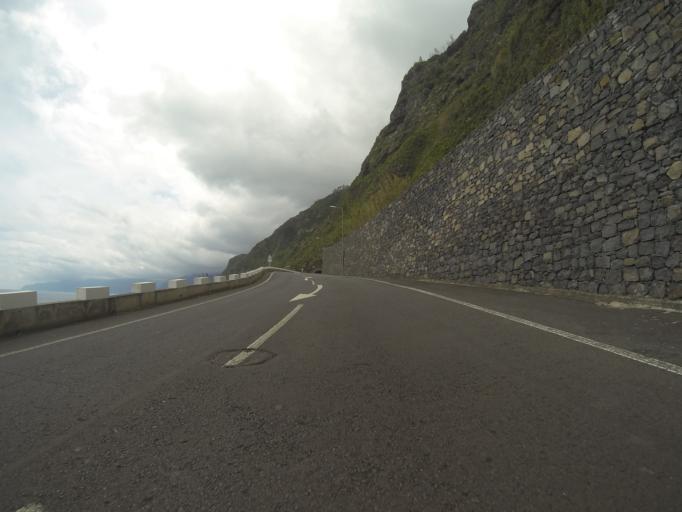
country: PT
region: Madeira
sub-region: Porto Moniz
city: Porto Moniz
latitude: 32.8604
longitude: -17.1642
